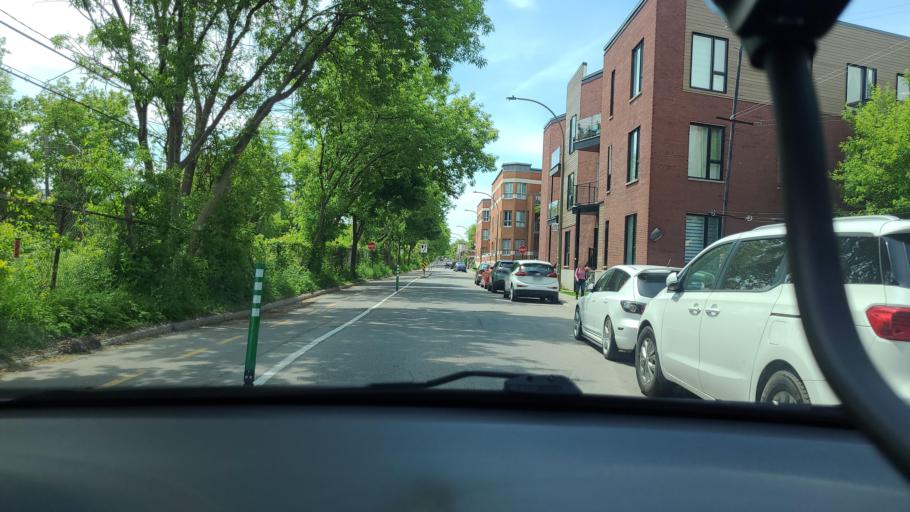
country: CA
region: Quebec
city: Saint-Raymond
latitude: 45.4699
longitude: -73.6108
